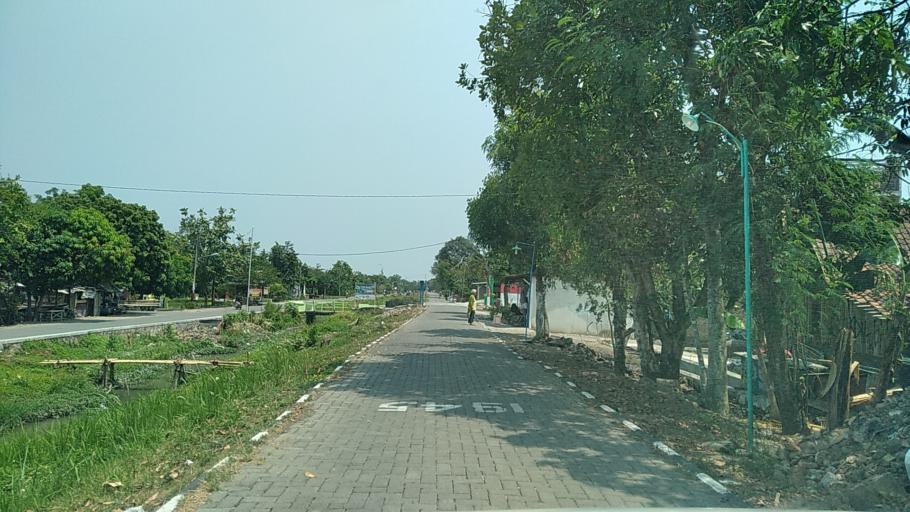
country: ID
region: Central Java
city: Mranggen
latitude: -7.0302
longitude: 110.4812
